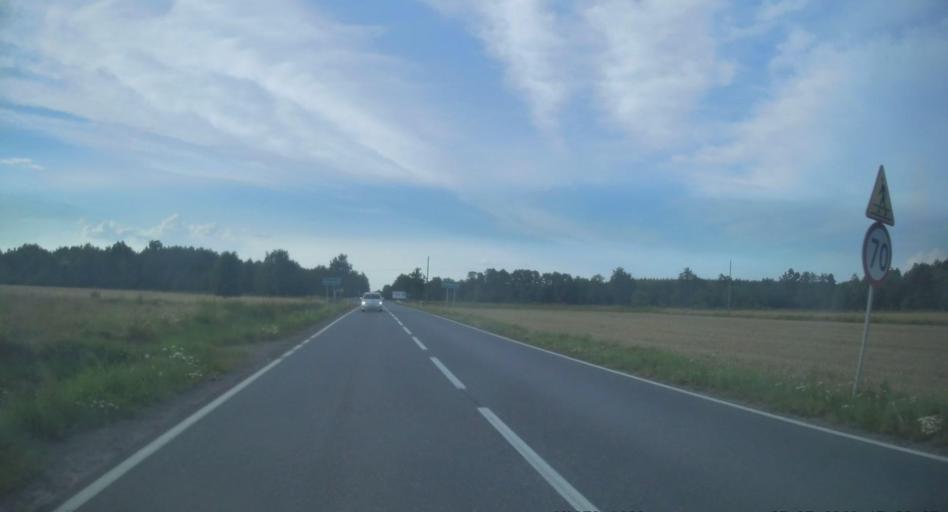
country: PL
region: Lesser Poland Voivodeship
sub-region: Powiat brzeski
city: Szczurowa
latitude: 50.0764
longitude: 20.6339
